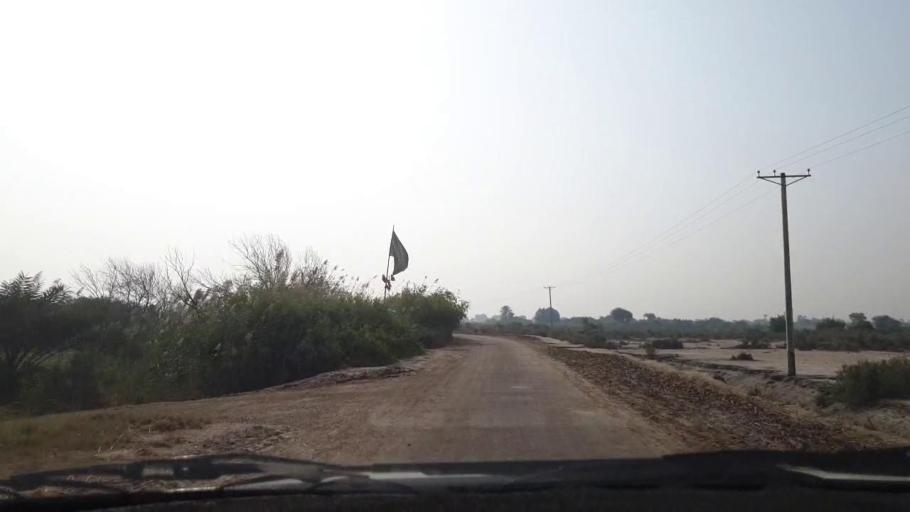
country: PK
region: Sindh
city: Tando Muhammad Khan
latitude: 25.0186
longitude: 68.4500
